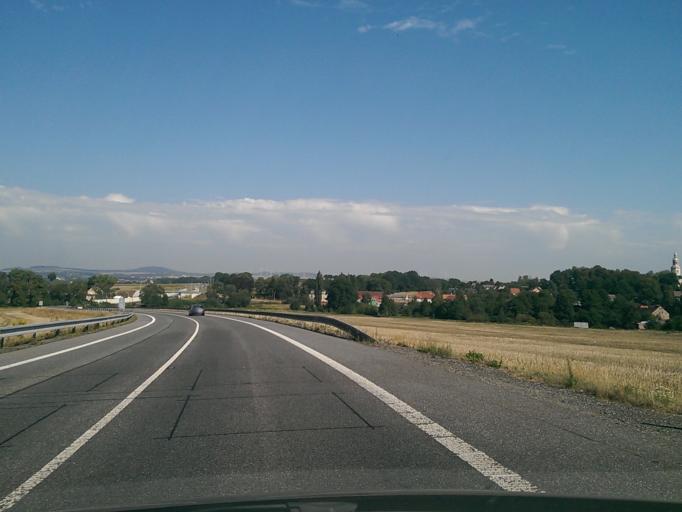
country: CZ
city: Hradek nad Nisou
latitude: 50.8656
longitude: 14.8497
